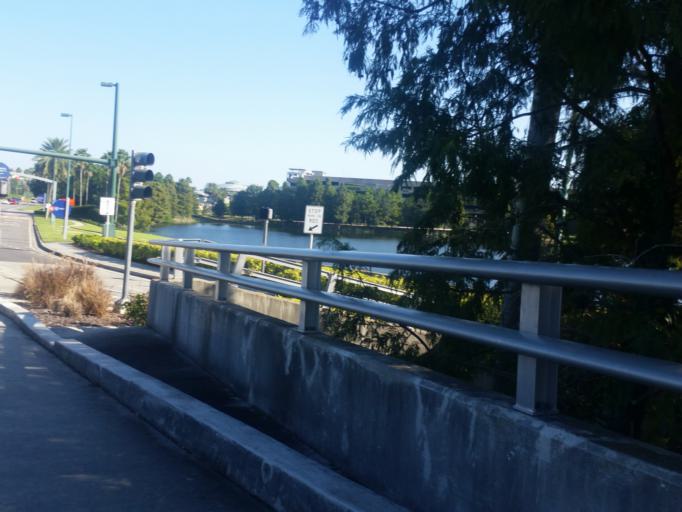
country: US
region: Florida
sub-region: Orange County
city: Tangelo Park
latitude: 28.4685
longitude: -81.4648
